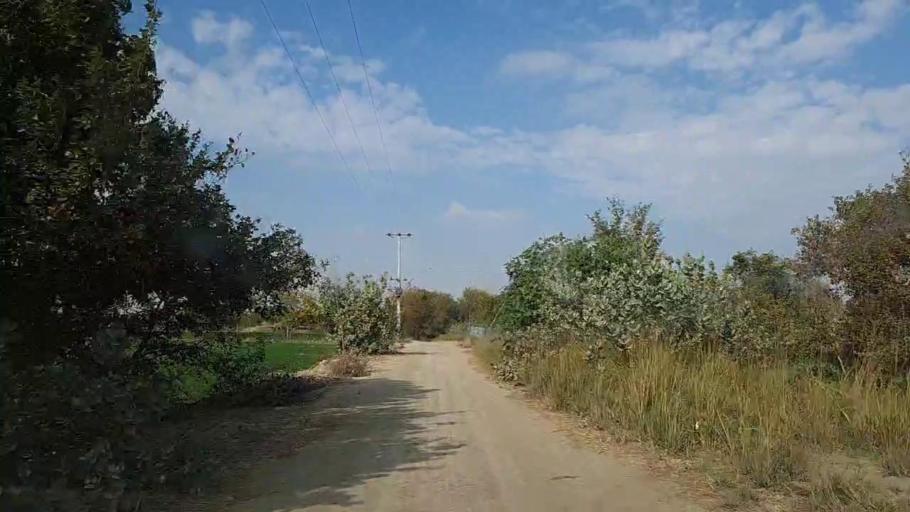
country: PK
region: Sindh
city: Sanghar
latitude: 26.2774
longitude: 69.0092
